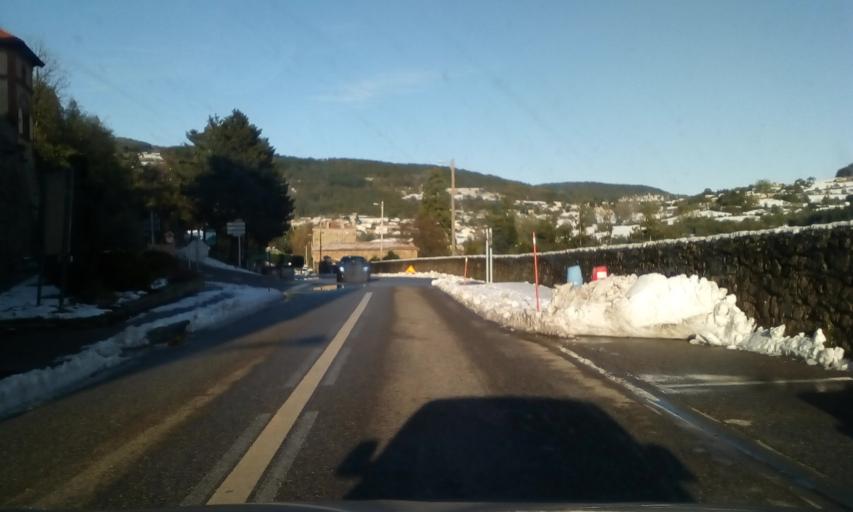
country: FR
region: Rhone-Alpes
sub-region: Departement de l'Ardeche
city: Saint-Felicien
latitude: 45.0880
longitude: 4.6282
